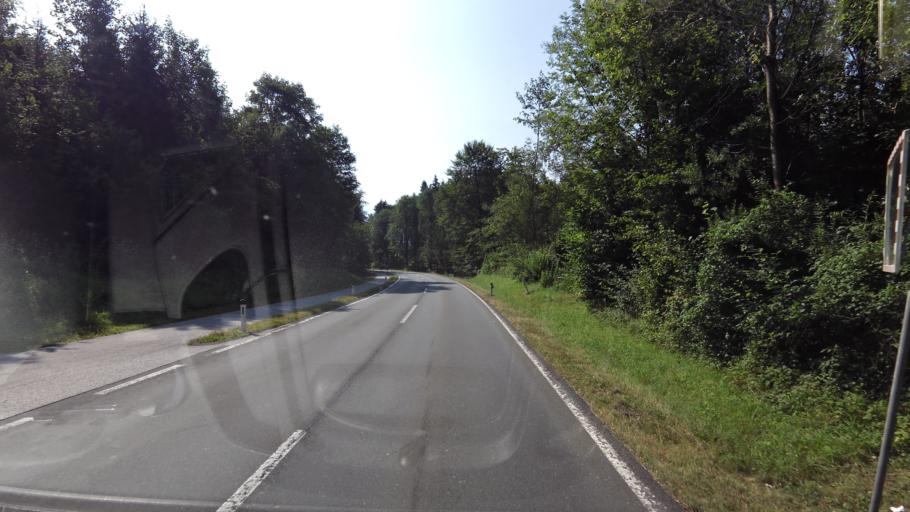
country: AT
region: Salzburg
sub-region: Politischer Bezirk Hallein
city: Adnet
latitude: 47.6581
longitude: 13.1254
